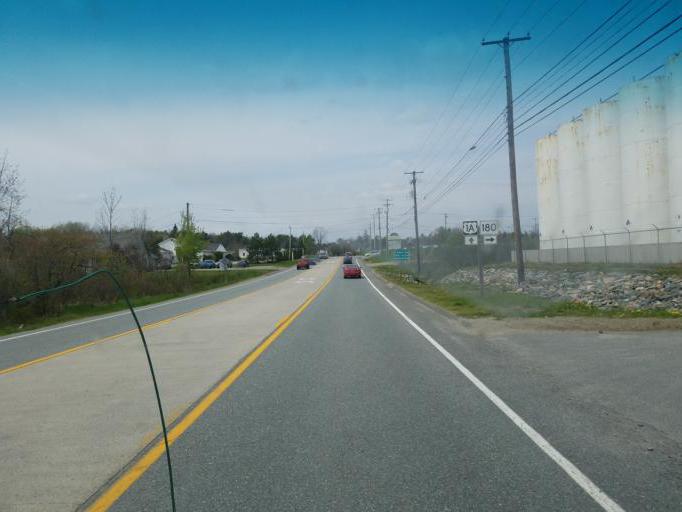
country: US
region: Maine
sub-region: Hancock County
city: Ellsworth
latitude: 44.5682
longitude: -68.4521
